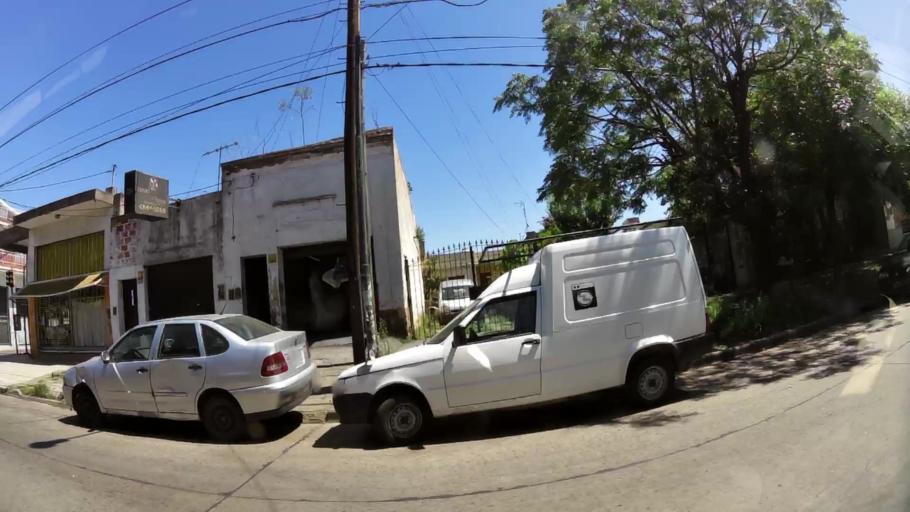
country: AR
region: Buenos Aires
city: Caseros
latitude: -34.5753
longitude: -58.5666
